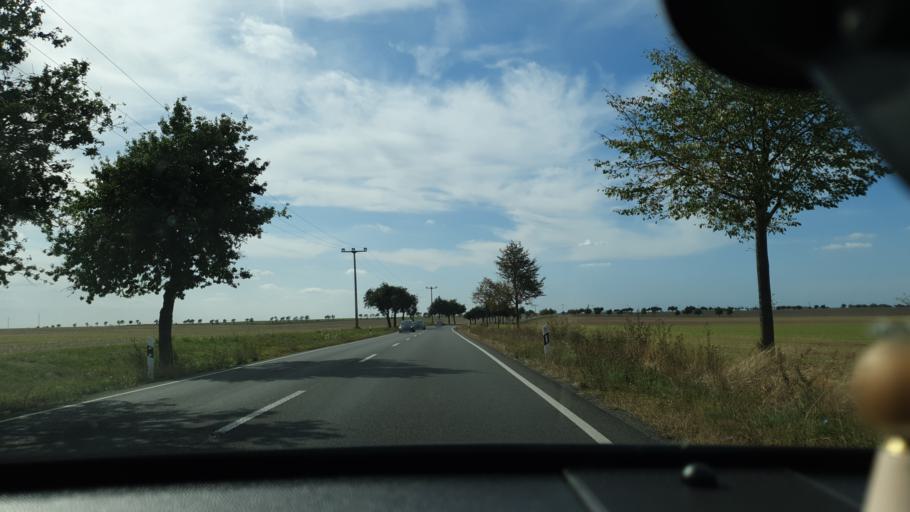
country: DE
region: Saxony
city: Krostitz
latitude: 51.4553
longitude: 12.5088
